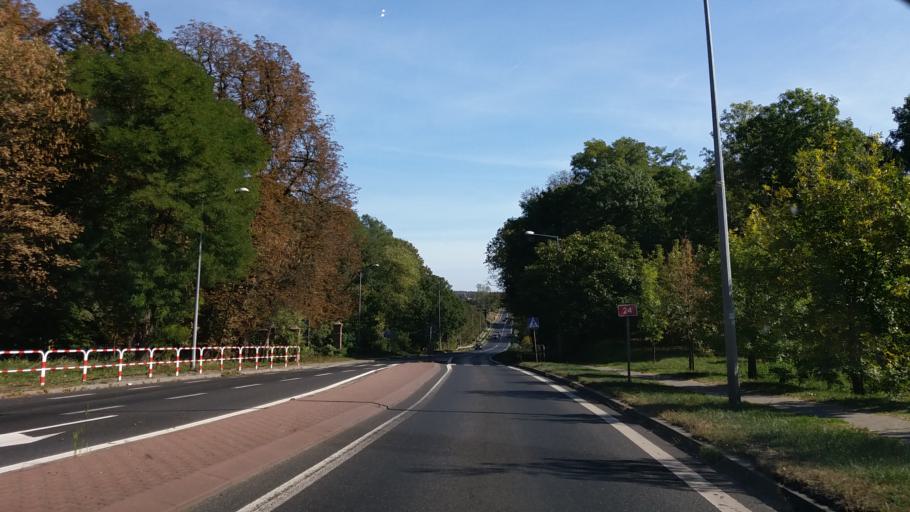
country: PL
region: Greater Poland Voivodeship
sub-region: Powiat miedzychodzki
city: Kwilcz
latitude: 52.5548
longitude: 16.0862
